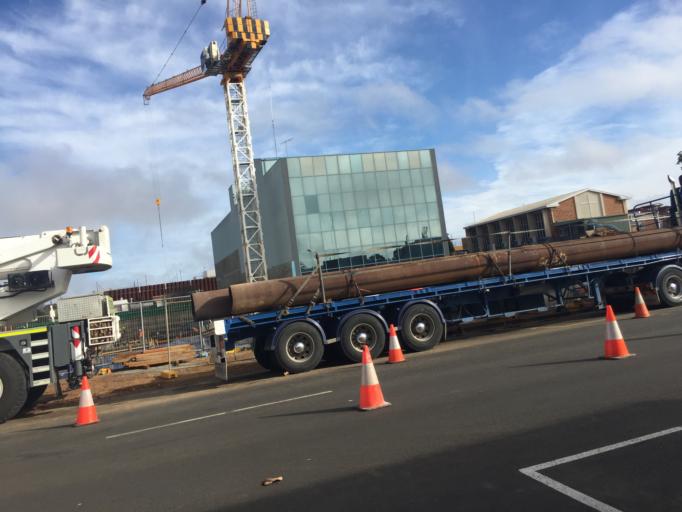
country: AU
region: Queensland
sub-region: Toowoomba
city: Toowoomba
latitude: -27.5633
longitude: 151.9541
